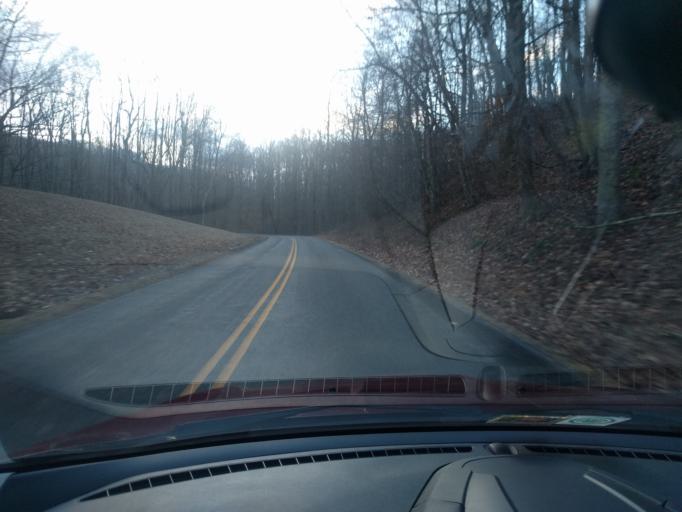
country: US
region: Virginia
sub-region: Botetourt County
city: Buchanan
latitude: 37.4564
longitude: -79.6290
